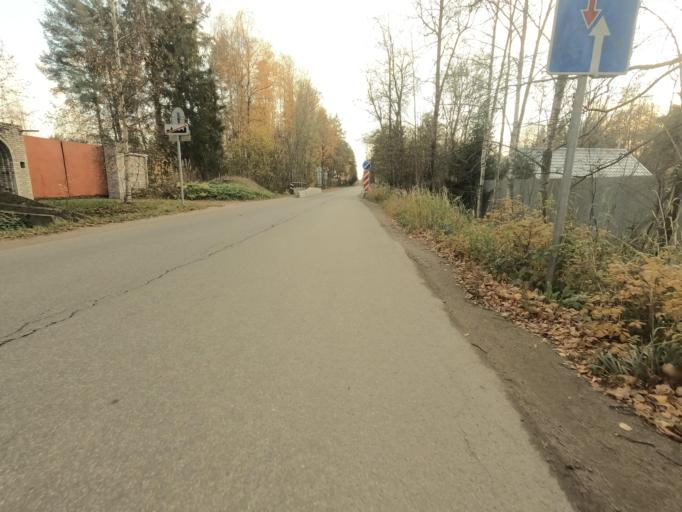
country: RU
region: St.-Petersburg
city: Beloostrov
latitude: 60.1673
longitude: 30.0108
